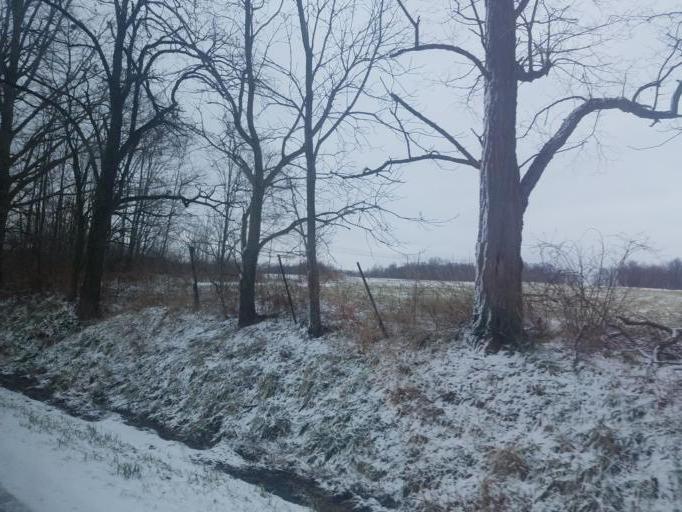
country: US
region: Ohio
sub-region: Delaware County
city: Sunbury
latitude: 40.2118
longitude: -82.7704
